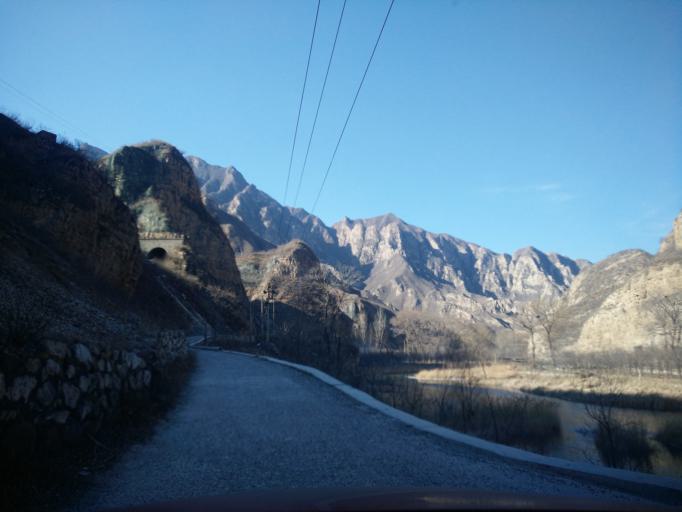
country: CN
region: Beijing
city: Yanjiatai
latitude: 40.1661
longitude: 115.6563
